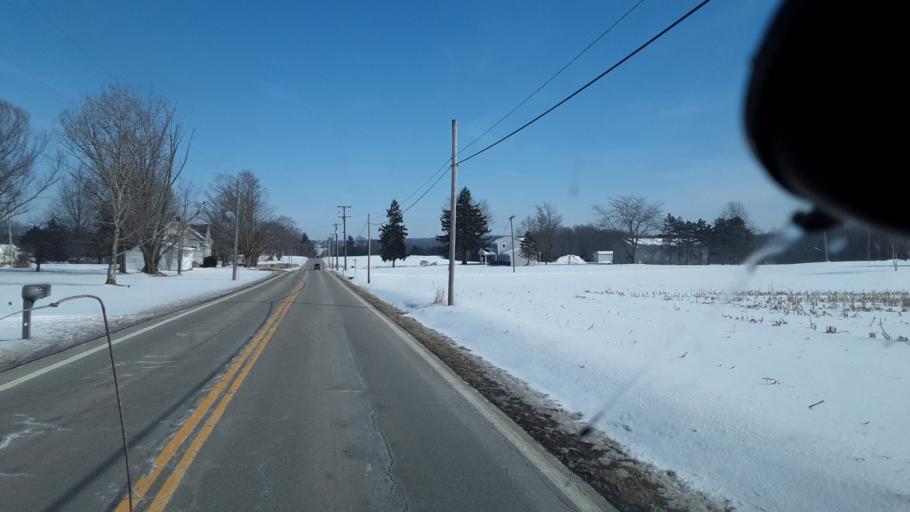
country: US
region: Ohio
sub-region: Columbiana County
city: Salem
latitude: 40.9447
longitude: -80.8995
